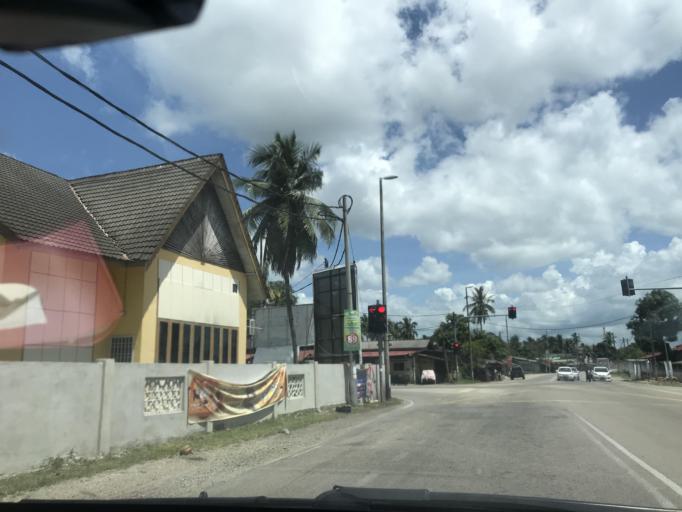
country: MY
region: Kelantan
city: Tumpat
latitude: 6.2193
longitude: 102.1135
